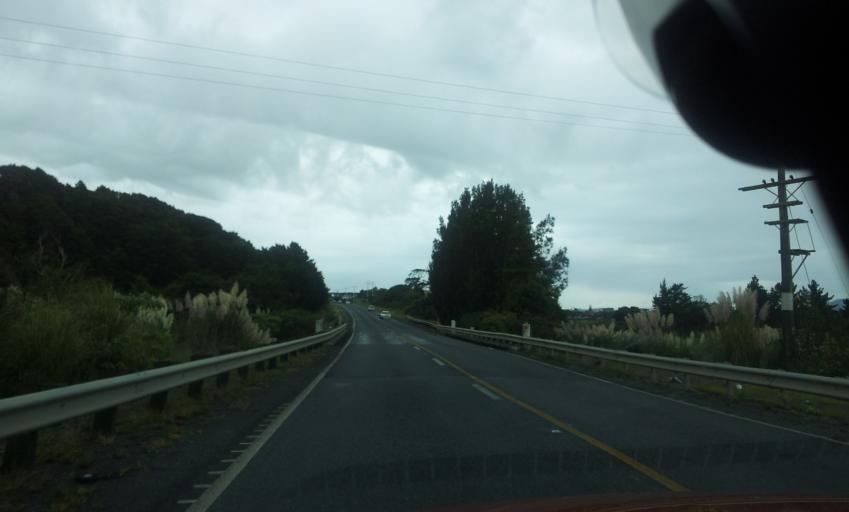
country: NZ
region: Northland
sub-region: Whangarei
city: Ruakaka
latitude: -35.9199
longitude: 174.4530
